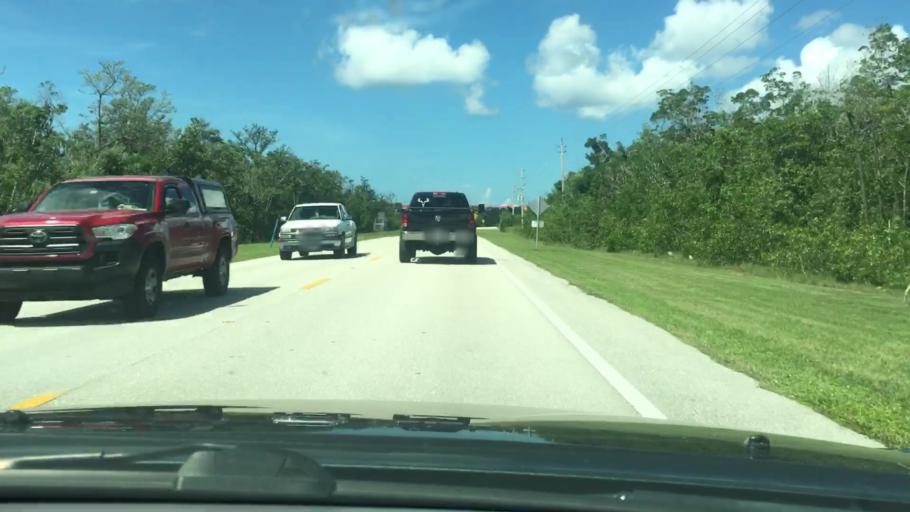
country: US
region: Florida
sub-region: Collier County
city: Marco
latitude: 25.9318
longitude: -81.6693
